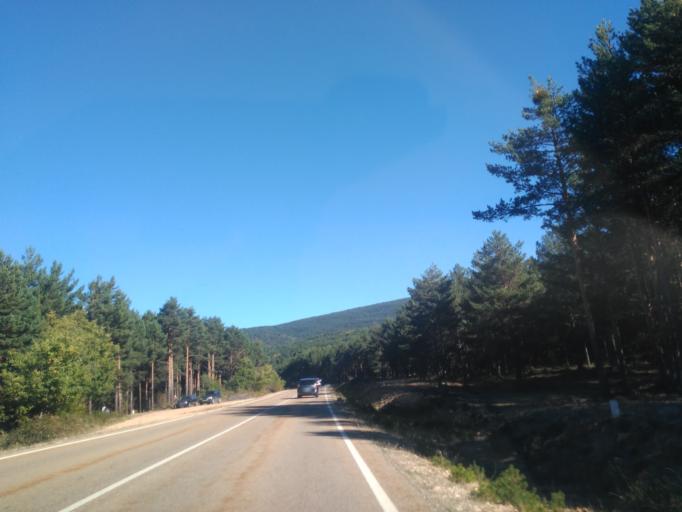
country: ES
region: Castille and Leon
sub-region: Provincia de Soria
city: Vinuesa
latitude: 41.9575
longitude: -2.7769
